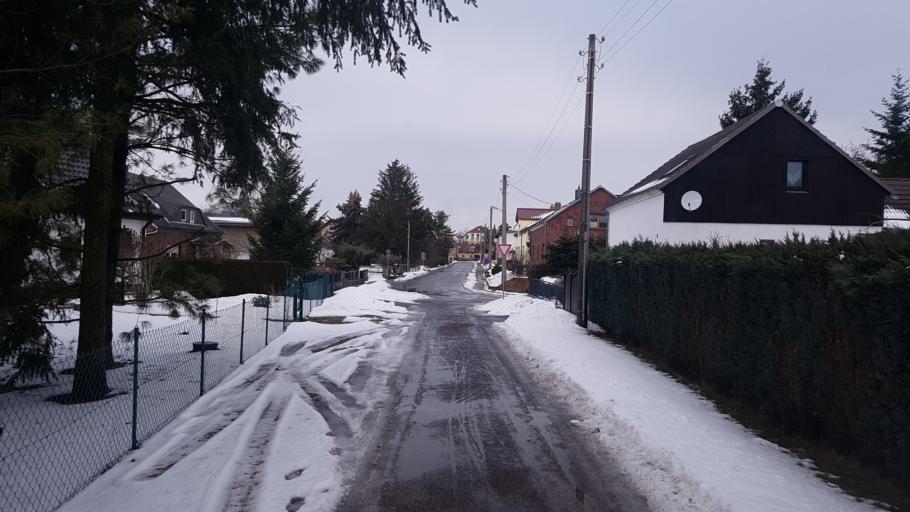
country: DE
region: Brandenburg
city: Grossraschen
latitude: 51.5850
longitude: 14.0158
